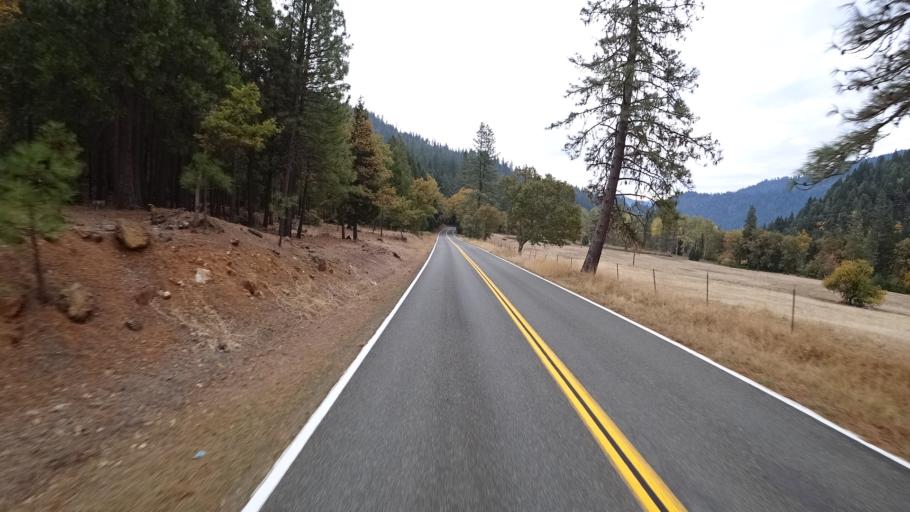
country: US
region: California
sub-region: Siskiyou County
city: Happy Camp
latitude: 41.8736
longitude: -123.4105
